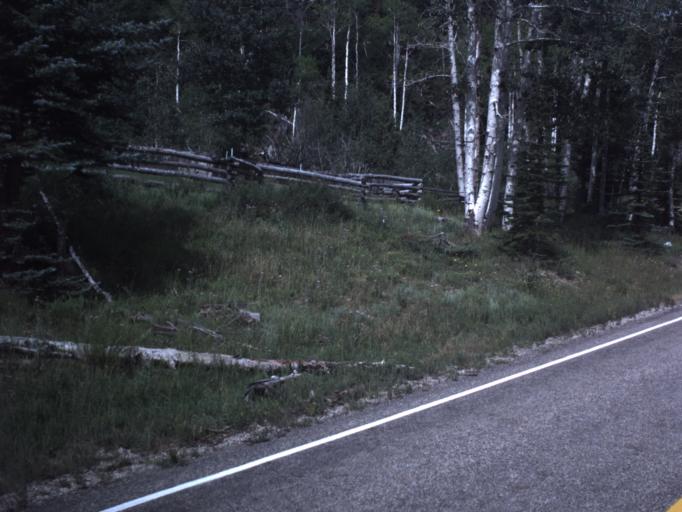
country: US
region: Utah
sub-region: Iron County
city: Cedar City
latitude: 37.5984
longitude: -112.9294
